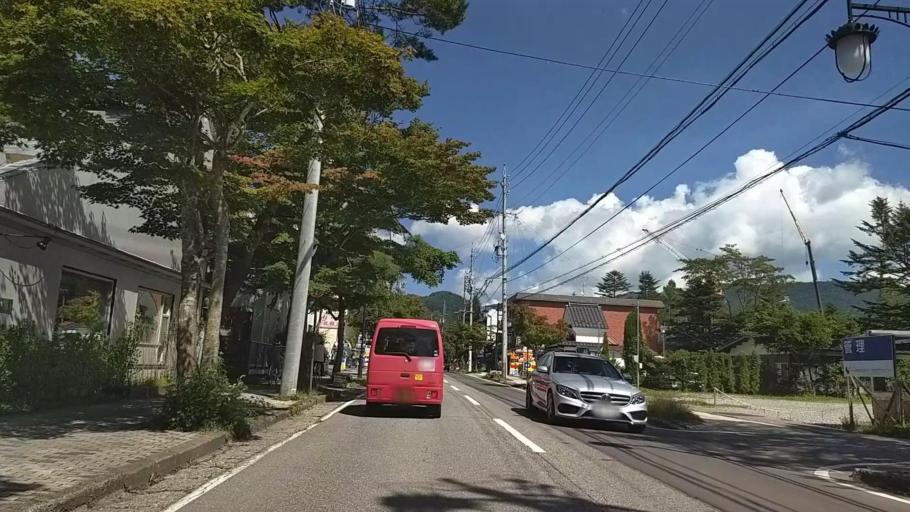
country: JP
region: Nagano
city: Saku
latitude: 36.3500
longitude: 138.6343
